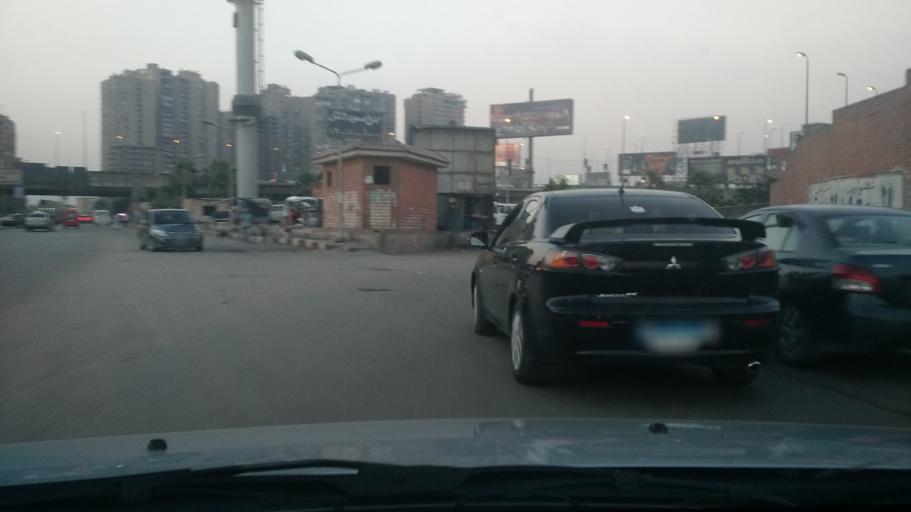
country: EG
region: Al Jizah
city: Al Jizah
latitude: 29.9849
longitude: 31.2132
